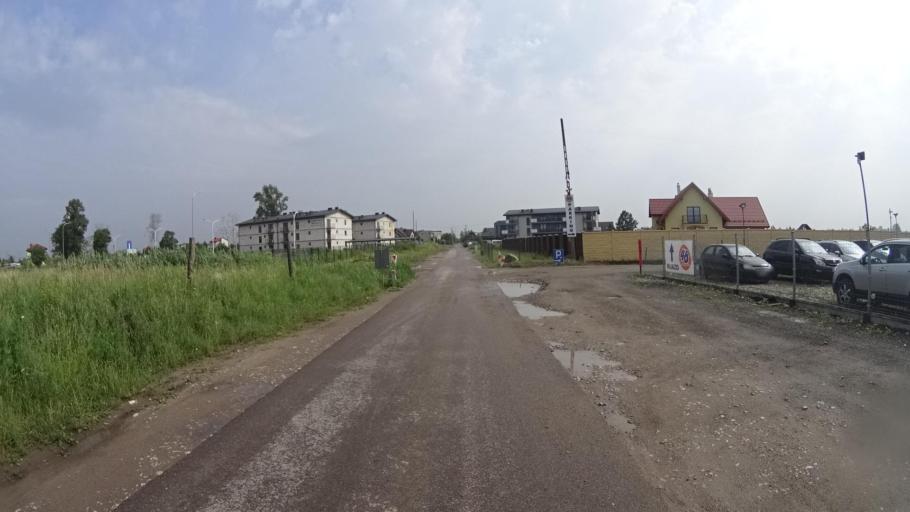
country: PL
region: Masovian Voivodeship
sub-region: Powiat pruszkowski
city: Raszyn
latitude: 52.1676
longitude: 20.9197
